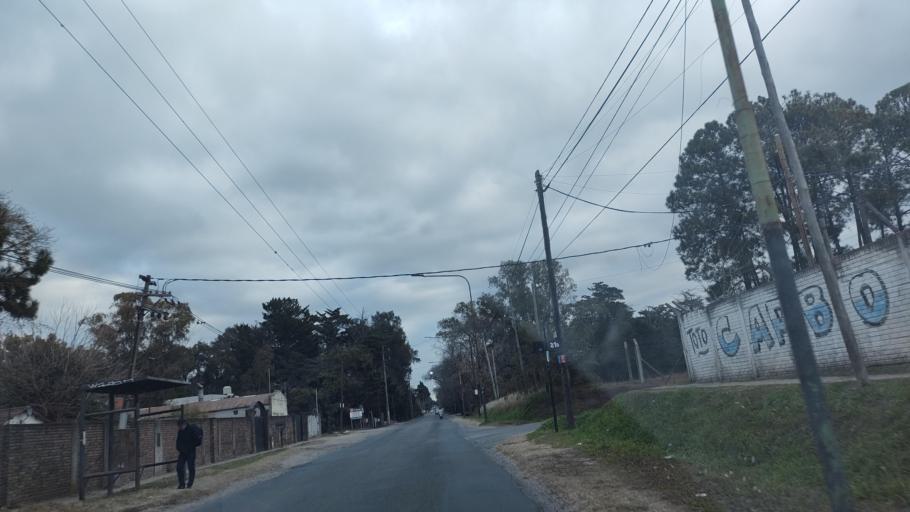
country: AR
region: Buenos Aires
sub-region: Partido de La Plata
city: La Plata
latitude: -34.8643
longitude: -58.0917
